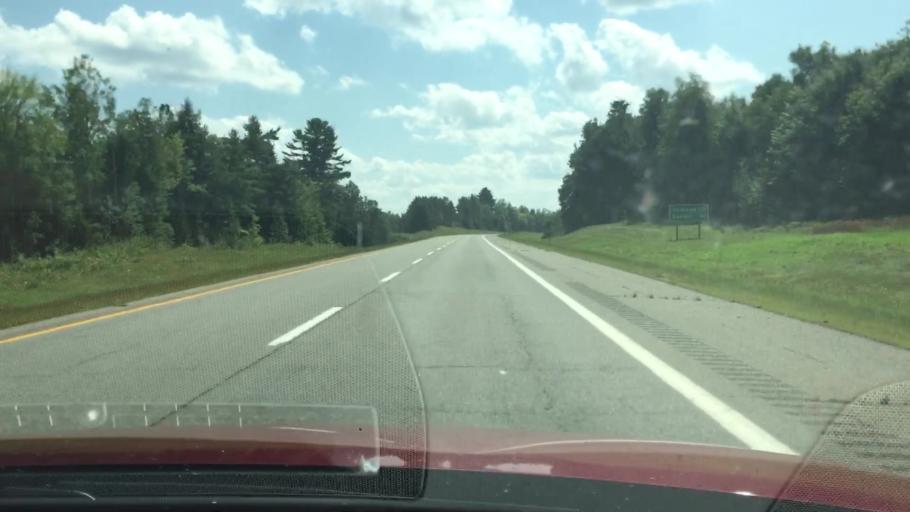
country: US
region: Maine
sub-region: Penobscot County
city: Lincoln
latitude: 45.3608
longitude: -68.6061
